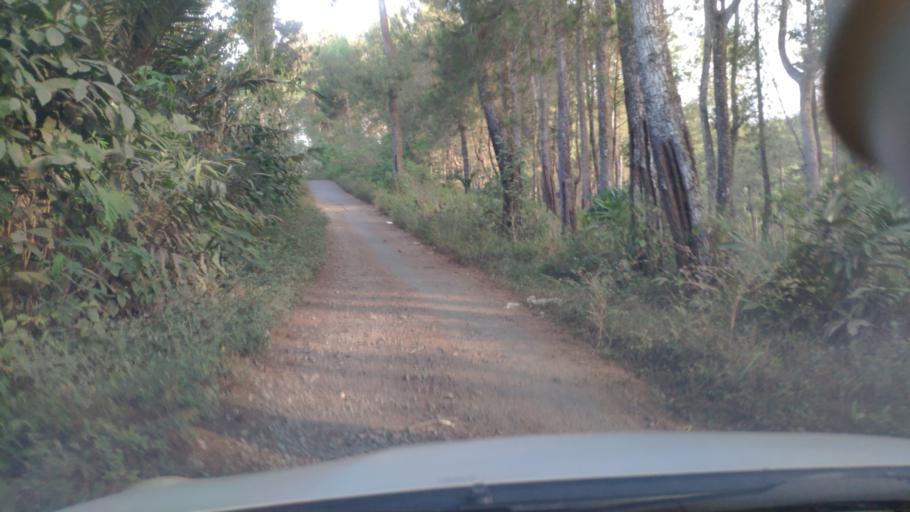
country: ID
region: Central Java
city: Wonosobo
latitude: -7.4345
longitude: 109.7532
